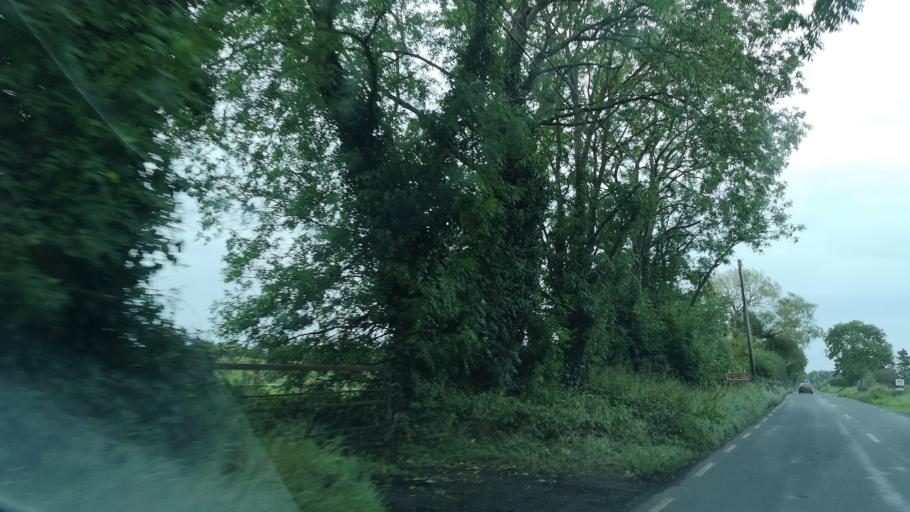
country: IE
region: Leinster
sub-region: Uibh Fhaili
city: Ferbane
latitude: 53.2283
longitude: -7.7933
